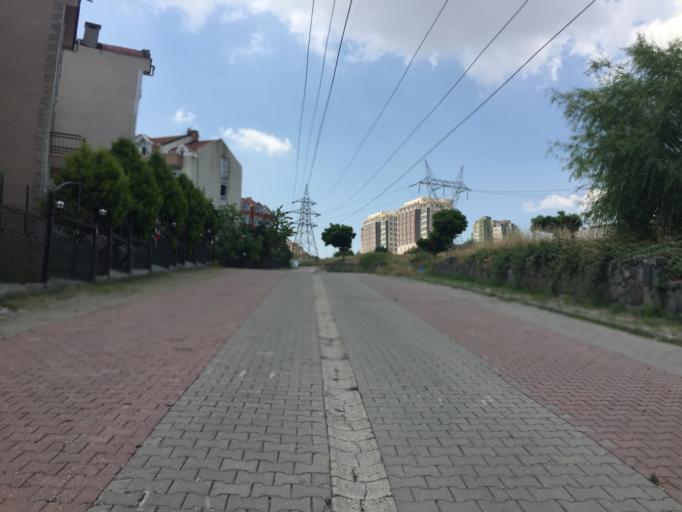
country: TR
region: Istanbul
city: Esenyurt
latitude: 41.0790
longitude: 28.6725
